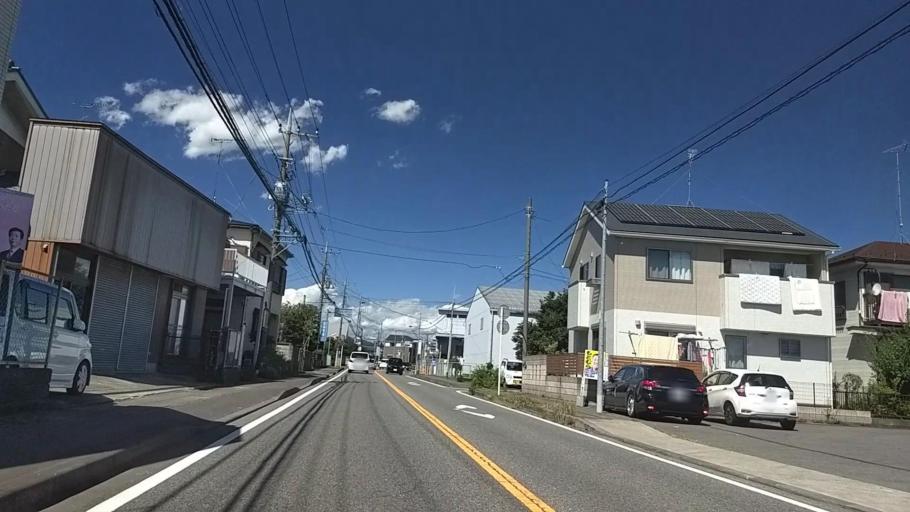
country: JP
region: Tokyo
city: Hachioji
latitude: 35.5749
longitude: 139.3166
